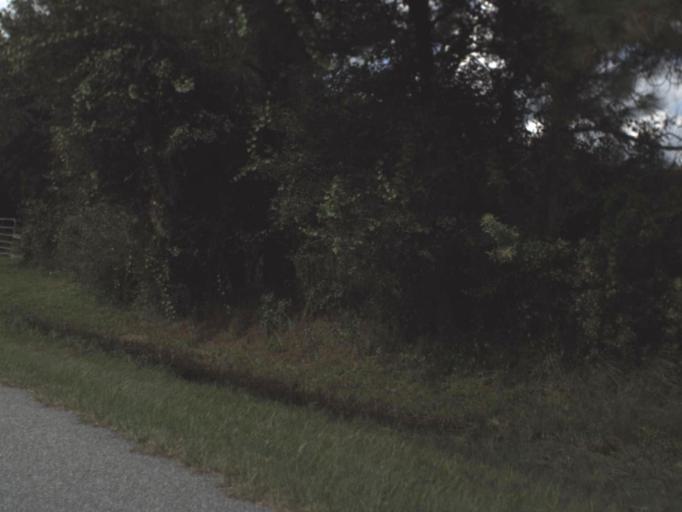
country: US
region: Florida
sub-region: DeSoto County
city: Arcadia
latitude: 27.3216
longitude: -82.1210
